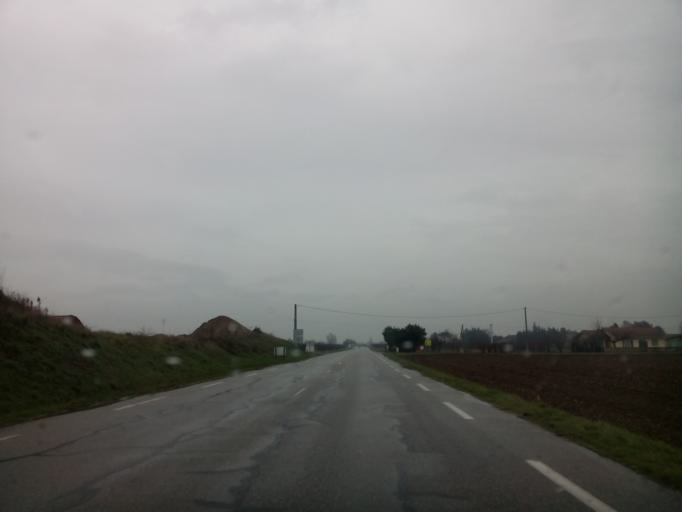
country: FR
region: Rhone-Alpes
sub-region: Departement de la Drome
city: Clerieux
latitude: 45.0491
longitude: 4.9890
